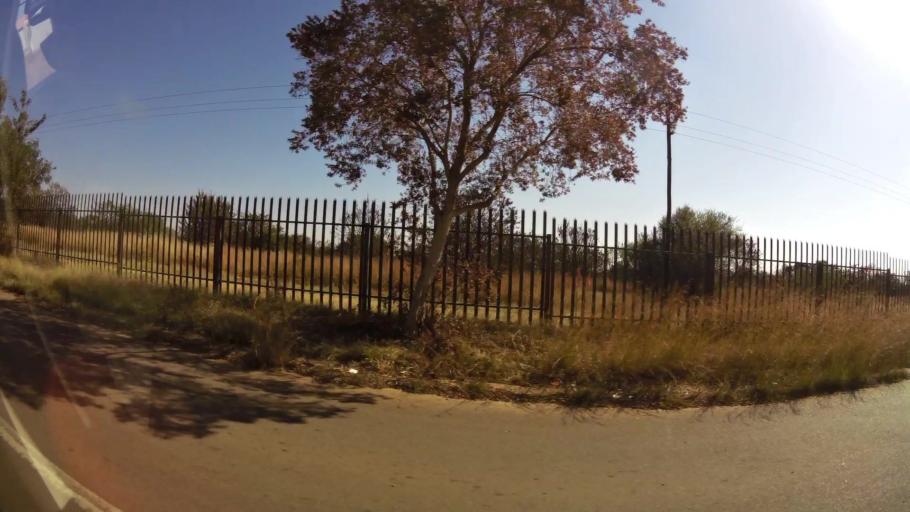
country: ZA
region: Gauteng
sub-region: City of Tshwane Metropolitan Municipality
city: Pretoria
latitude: -25.6510
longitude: 28.2631
